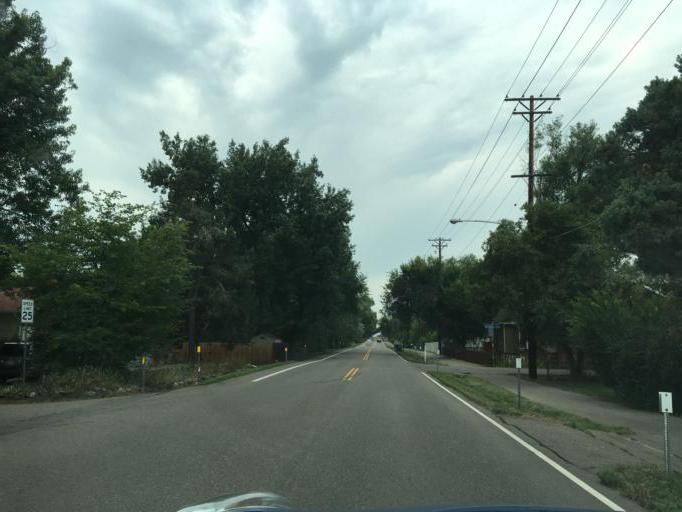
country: US
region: Colorado
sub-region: Jefferson County
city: Wheat Ridge
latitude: 39.7475
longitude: -105.0957
